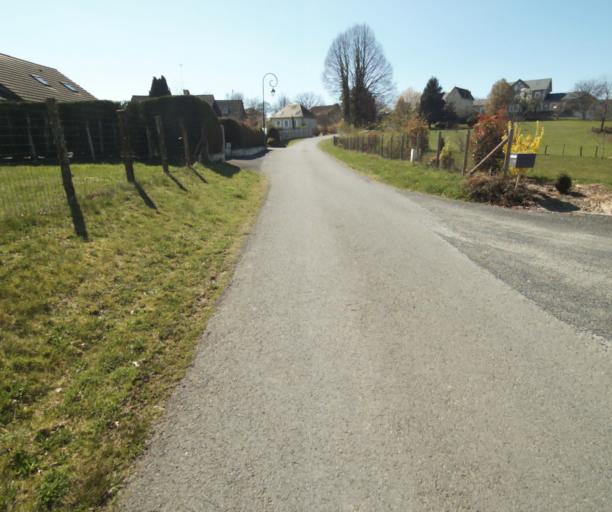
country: FR
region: Limousin
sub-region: Departement de la Correze
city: Saint-Mexant
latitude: 45.2860
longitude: 1.6602
